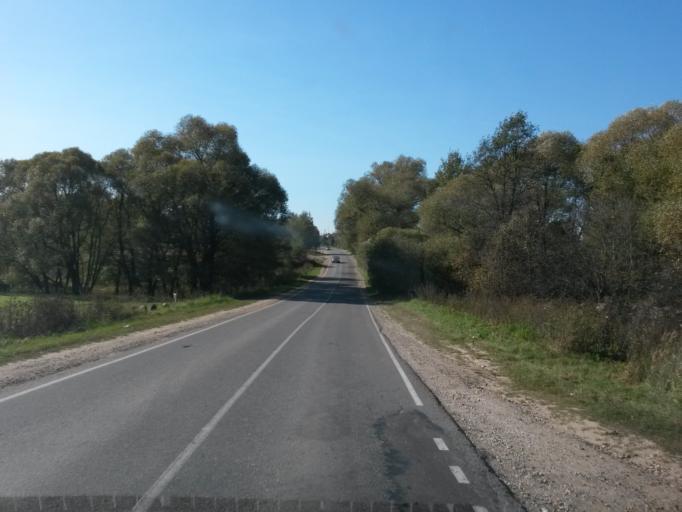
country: RU
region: Moskovskaya
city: Lyubuchany
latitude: 55.2592
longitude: 37.6049
